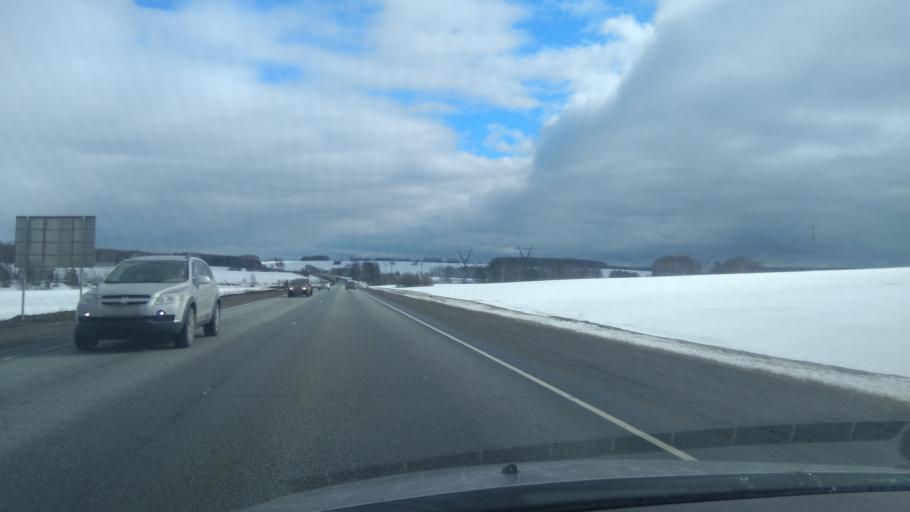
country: RU
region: Sverdlovsk
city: Ufimskiy
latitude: 56.7740
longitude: 58.0050
